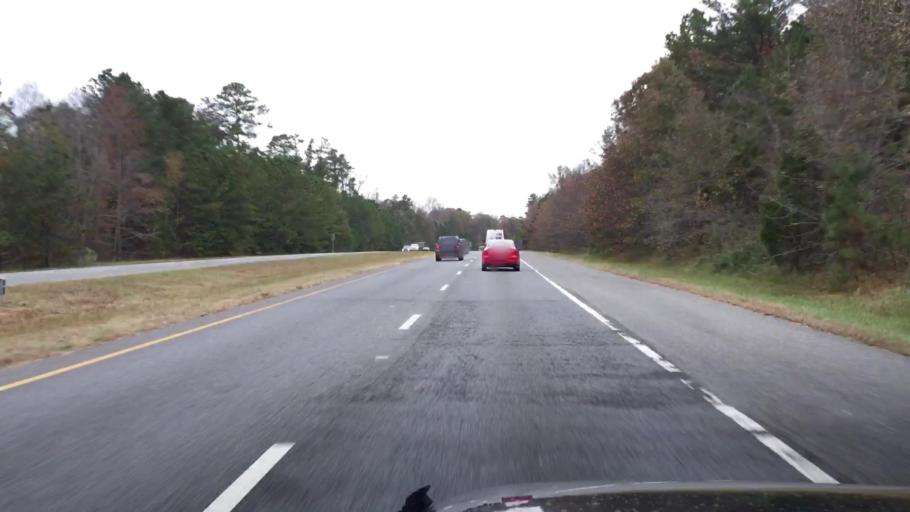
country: US
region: Virginia
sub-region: James City County
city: Williamsburg
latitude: 37.3113
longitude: -76.7474
